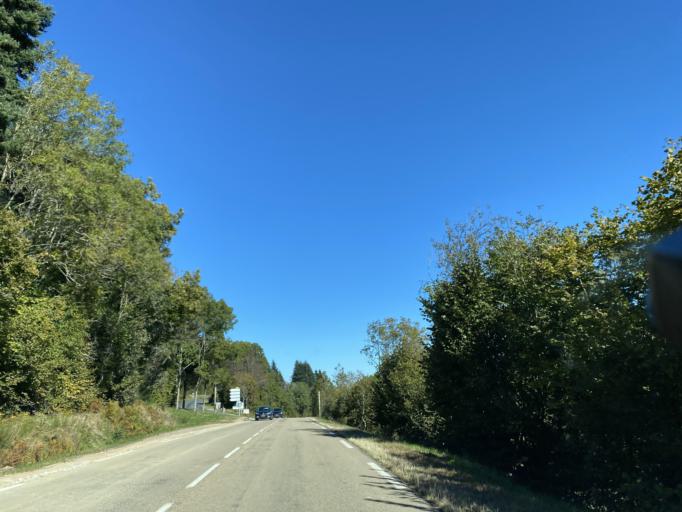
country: FR
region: Rhone-Alpes
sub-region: Departement de la Loire
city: Saint-Just-en-Chevalet
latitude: 45.9528
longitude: 3.8779
